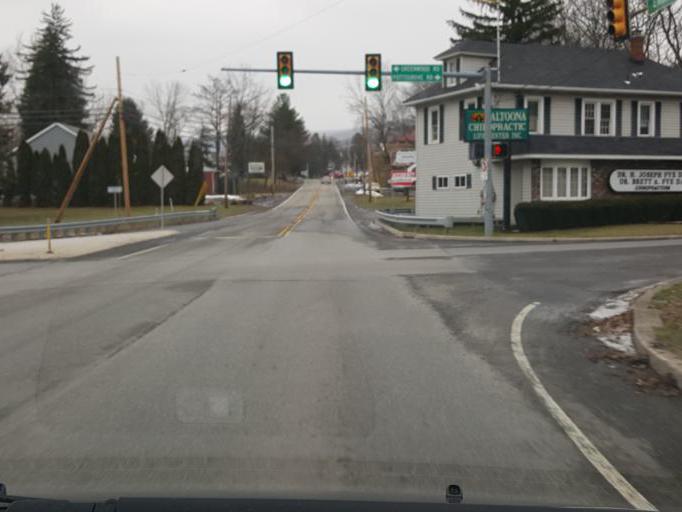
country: US
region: Pennsylvania
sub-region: Blair County
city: Greenwood
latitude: 40.5297
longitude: -78.3659
